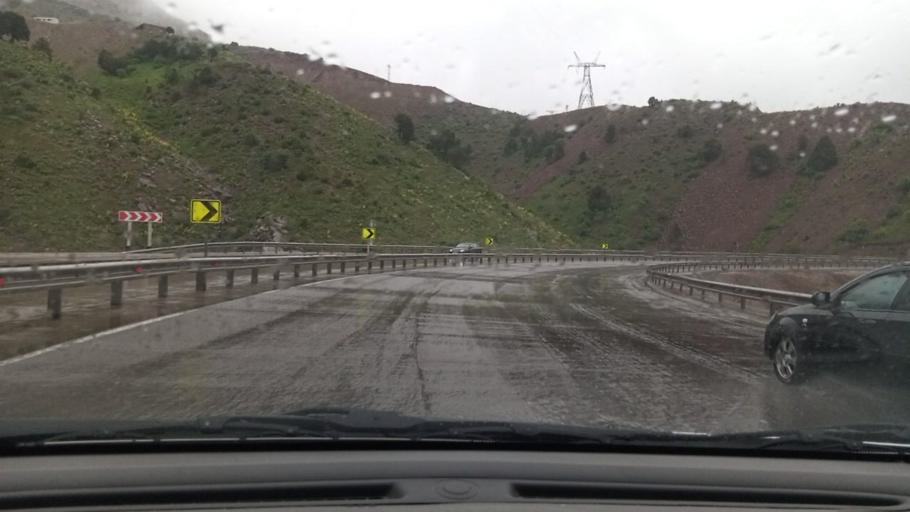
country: UZ
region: Toshkent
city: Angren
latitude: 41.0903
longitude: 70.5350
